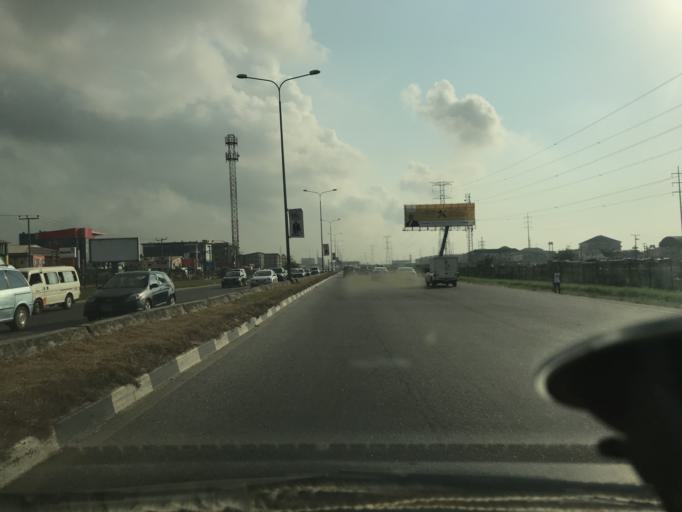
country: NG
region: Lagos
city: Ikoyi
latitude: 6.4321
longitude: 3.4767
